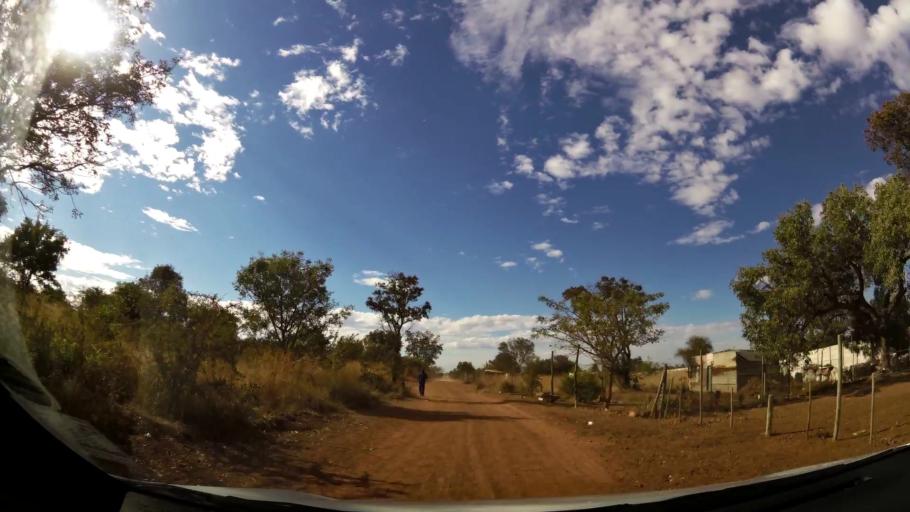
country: ZA
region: Limpopo
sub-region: Waterberg District Municipality
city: Warmbaths
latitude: -24.8752
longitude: 28.2746
